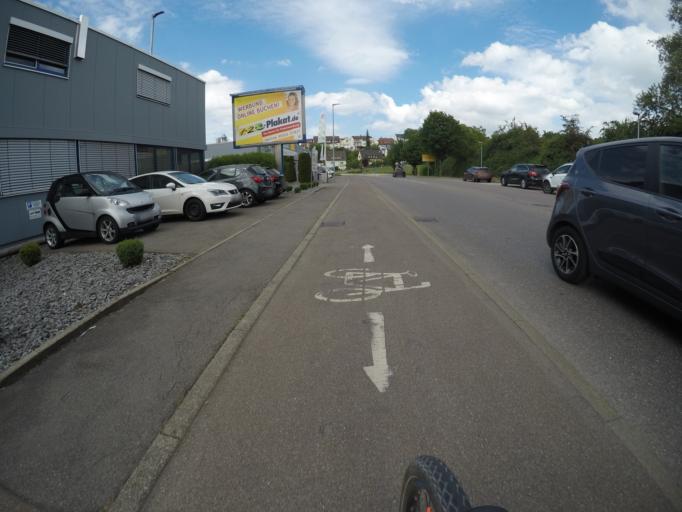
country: DE
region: Baden-Wuerttemberg
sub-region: Regierungsbezirk Stuttgart
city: Kongen
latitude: 48.6846
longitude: 9.3738
